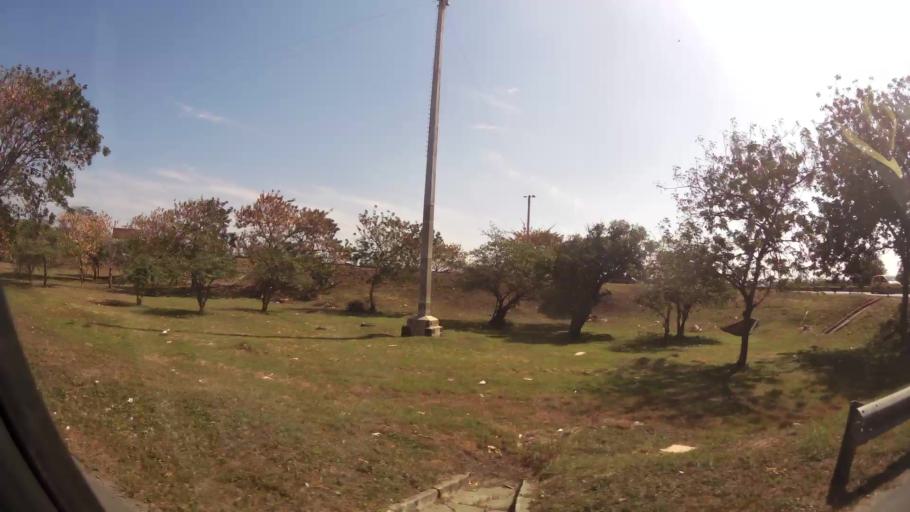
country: CO
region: Atlantico
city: Barranquilla
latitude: 10.9440
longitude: -74.8351
